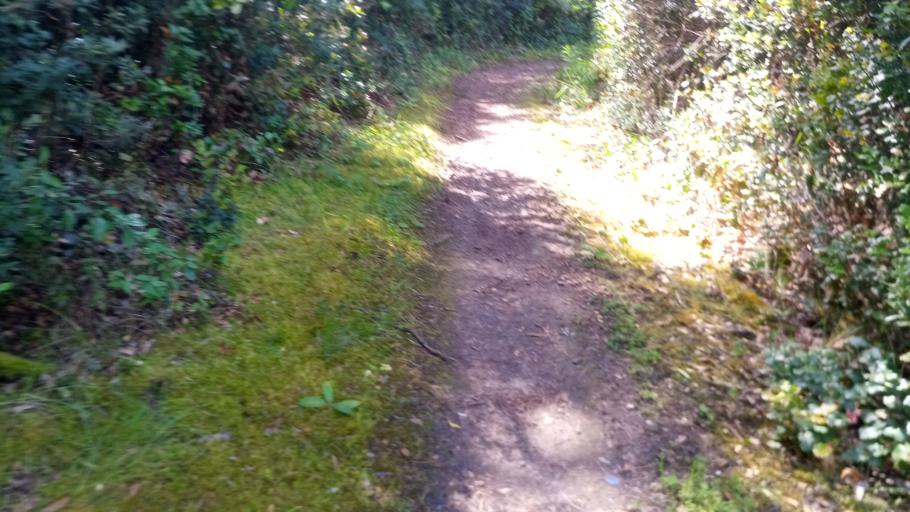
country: PT
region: Leiria
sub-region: Caldas da Rainha
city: Caldas da Rainha
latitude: 39.4020
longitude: -9.1895
